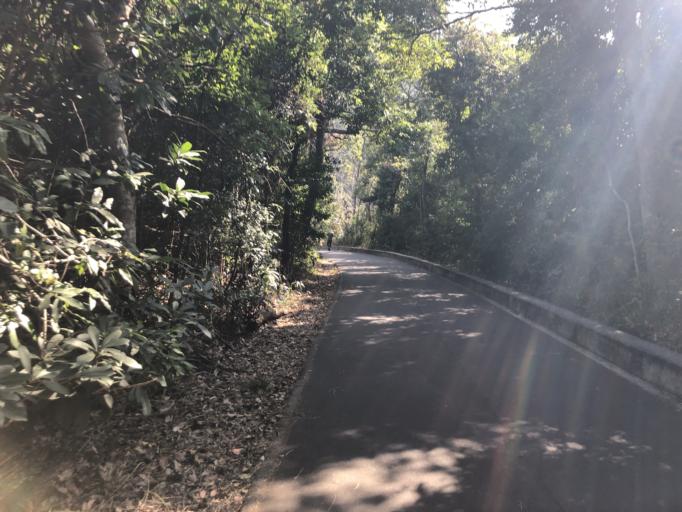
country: HK
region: Wanchai
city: Wan Chai
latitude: 22.2497
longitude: 114.2132
